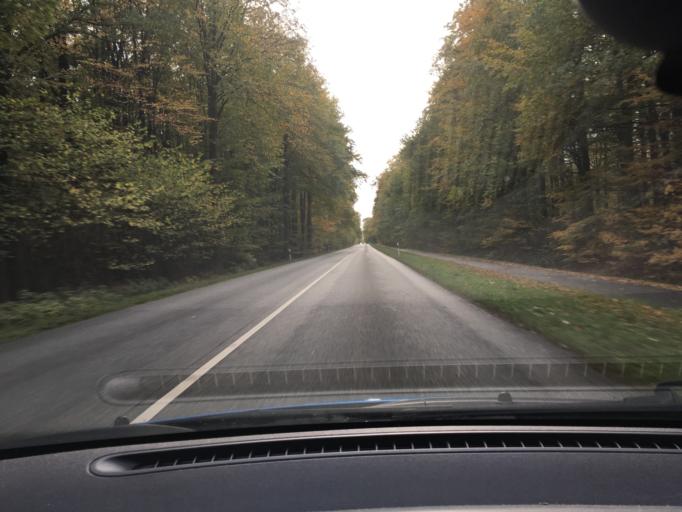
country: DE
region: Schleswig-Holstein
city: Sahms
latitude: 53.5390
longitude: 10.5304
